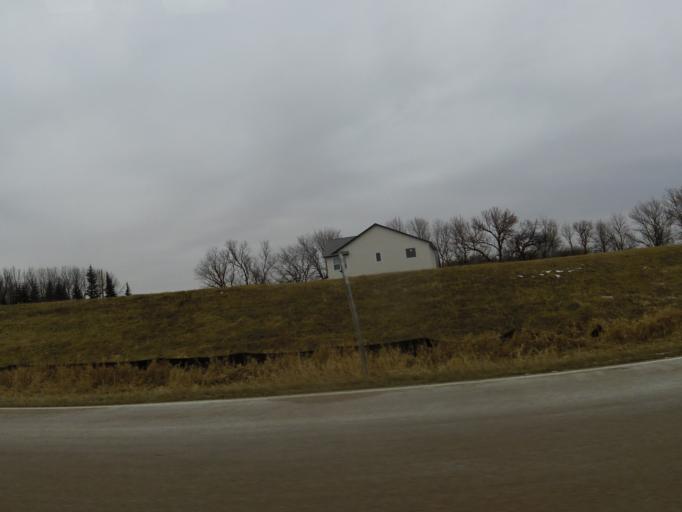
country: US
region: Minnesota
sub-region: Carver County
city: Watertown
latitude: 44.9633
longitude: -93.7975
